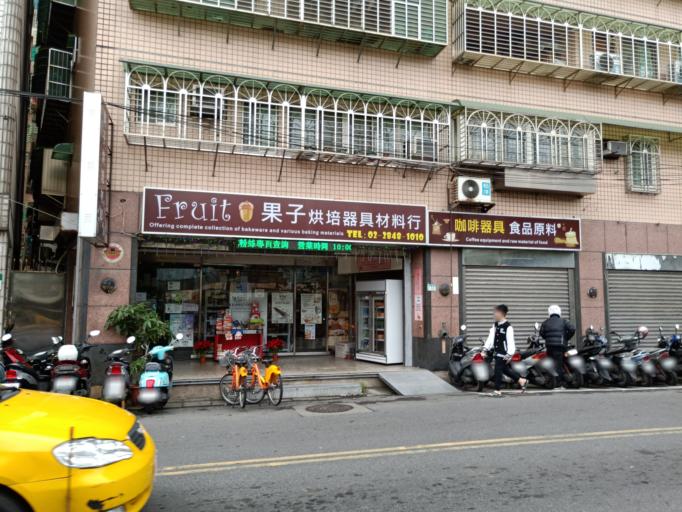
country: TW
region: Taipei
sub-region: Taipei
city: Banqiao
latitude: 25.0852
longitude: 121.4559
